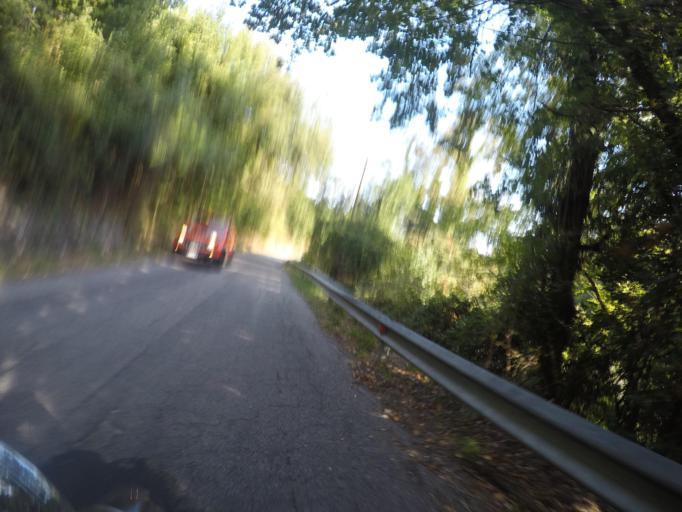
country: IT
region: Tuscany
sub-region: Provincia di Massa-Carrara
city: Carrara
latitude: 44.0846
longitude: 10.0901
